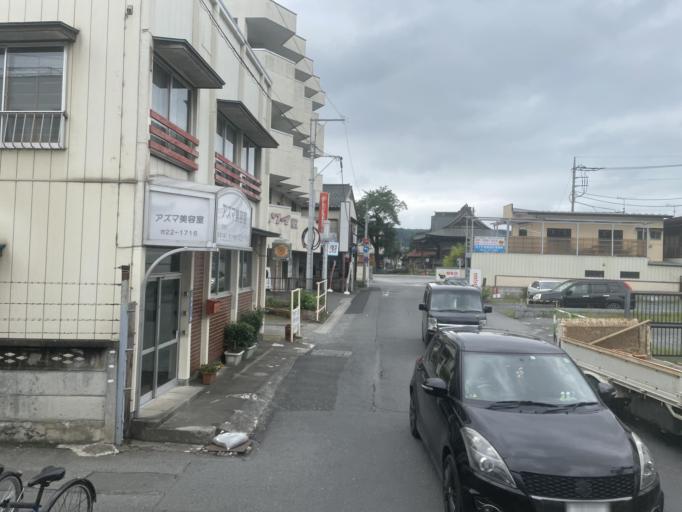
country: JP
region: Saitama
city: Chichibu
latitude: 35.9919
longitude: 139.0835
